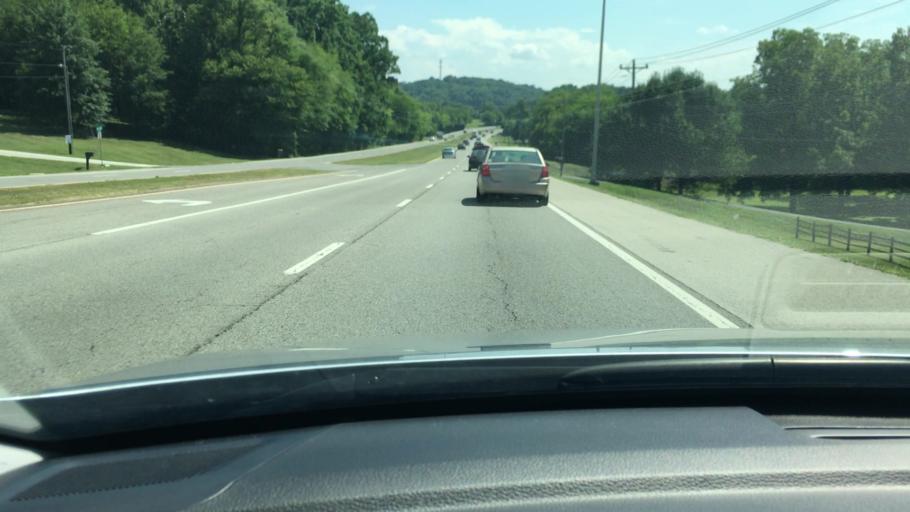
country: US
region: Tennessee
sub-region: Maury County
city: Columbia
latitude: 35.6807
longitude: -86.9984
